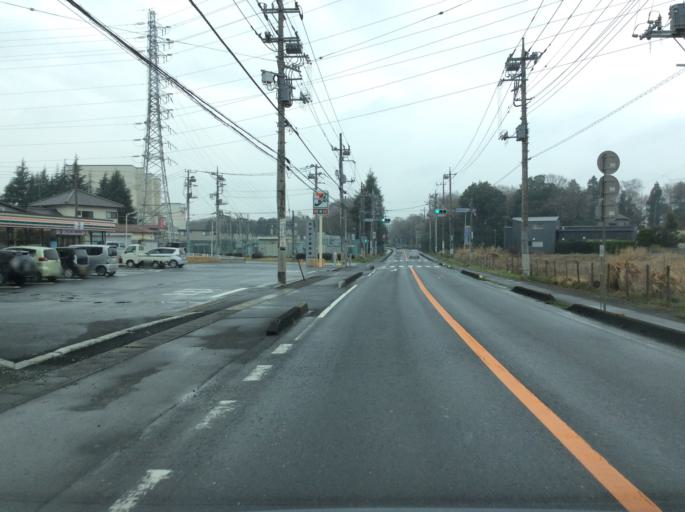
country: JP
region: Ibaraki
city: Mitsukaido
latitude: 35.9853
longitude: 139.9518
